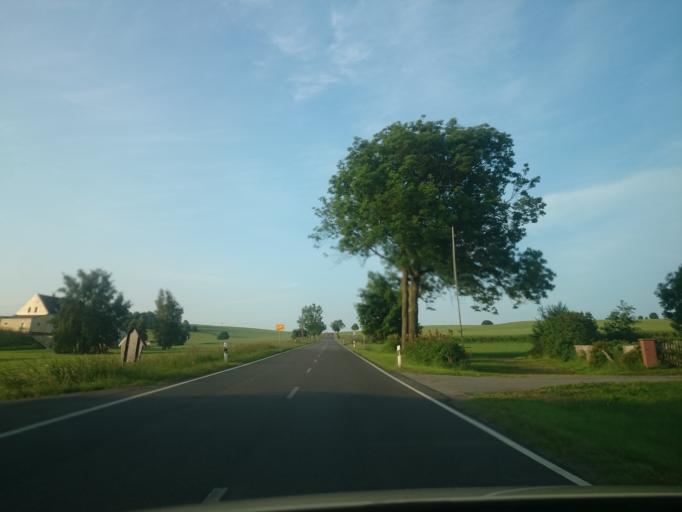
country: DE
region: Saxony
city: Grosshartmannsdorf
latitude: 50.7842
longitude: 13.3211
